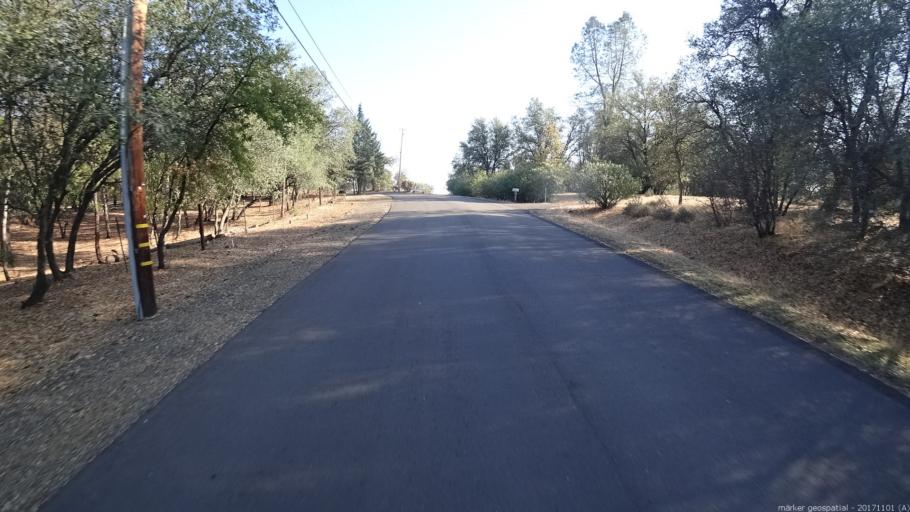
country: US
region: California
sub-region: Shasta County
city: Shasta Lake
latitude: 40.6763
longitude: -122.3006
